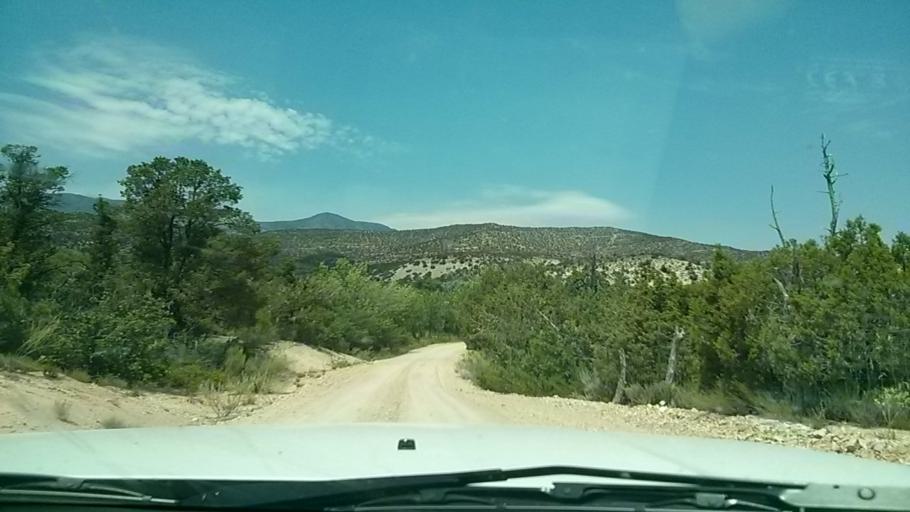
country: US
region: Utah
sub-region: Washington County
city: Toquerville
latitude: 37.2547
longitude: -113.4290
